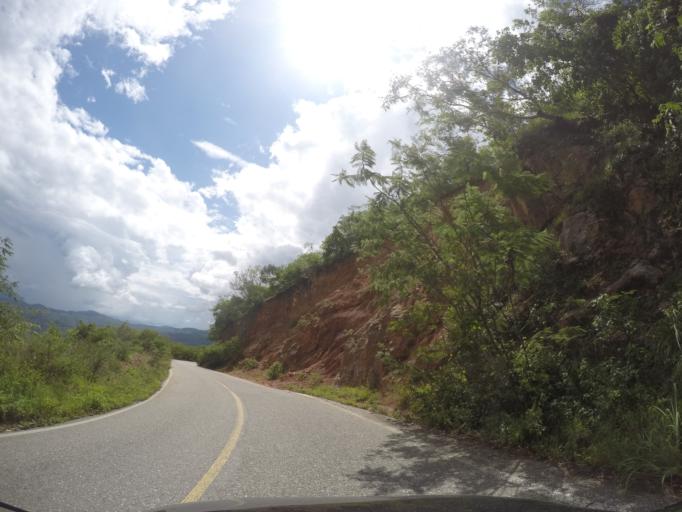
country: MX
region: Oaxaca
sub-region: San Jeronimo Coatlan
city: San Cristobal Honduras
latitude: 16.4336
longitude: -97.0484
